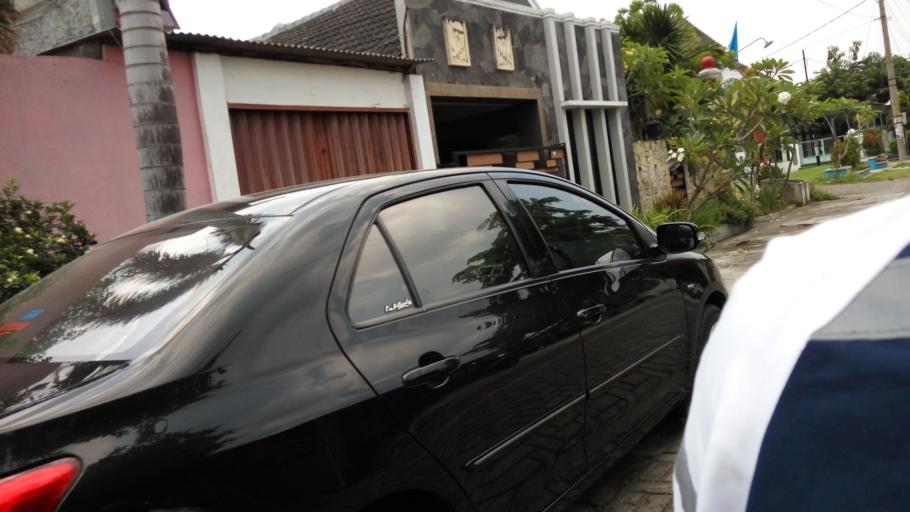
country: ID
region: Central Java
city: Mranggen
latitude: -7.0394
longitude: 110.4774
